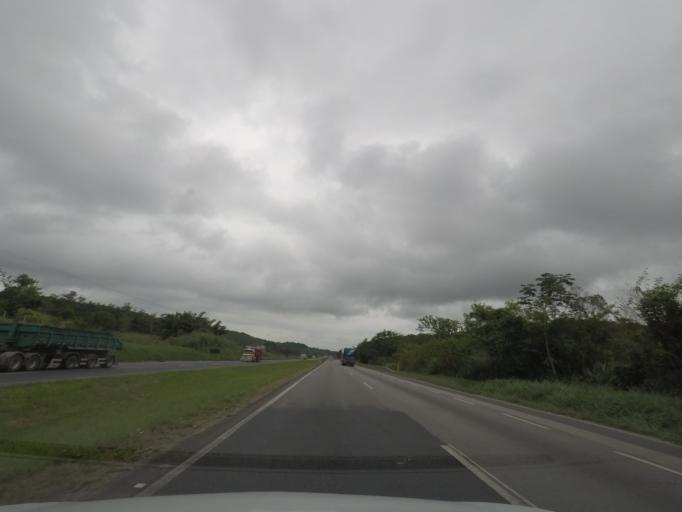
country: BR
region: Sao Paulo
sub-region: Registro
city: Registro
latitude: -24.4080
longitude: -47.7476
